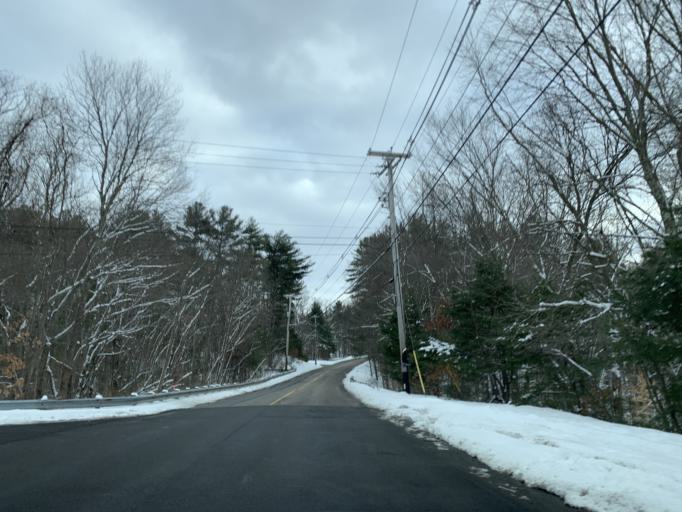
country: US
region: Massachusetts
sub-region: Norfolk County
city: Franklin
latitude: 42.0621
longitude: -71.4285
